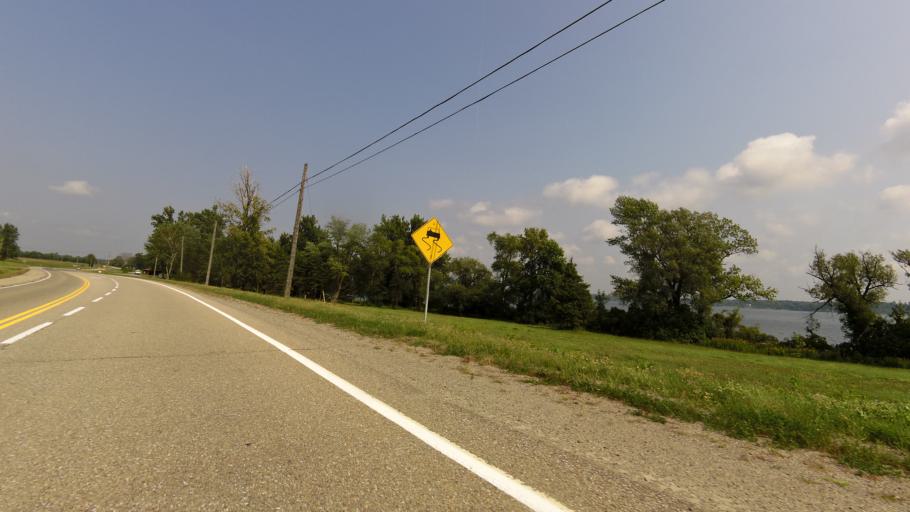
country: CA
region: Ontario
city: Prescott
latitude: 44.6647
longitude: -75.5730
